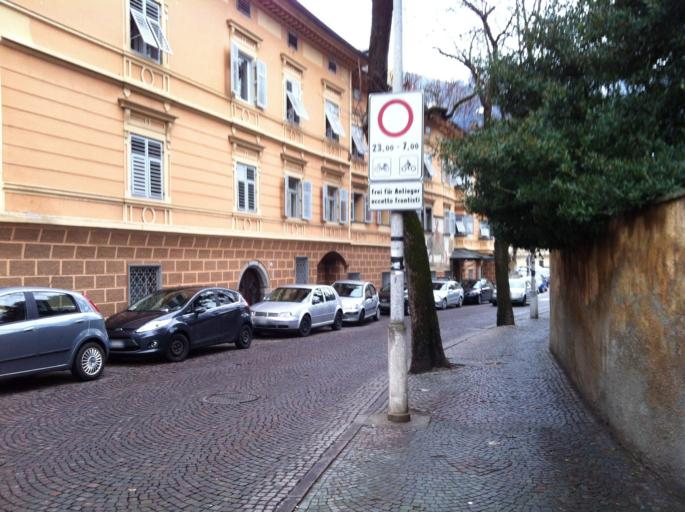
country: IT
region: Trentino-Alto Adige
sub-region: Bolzano
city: Bressanone
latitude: 46.7195
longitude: 11.6530
